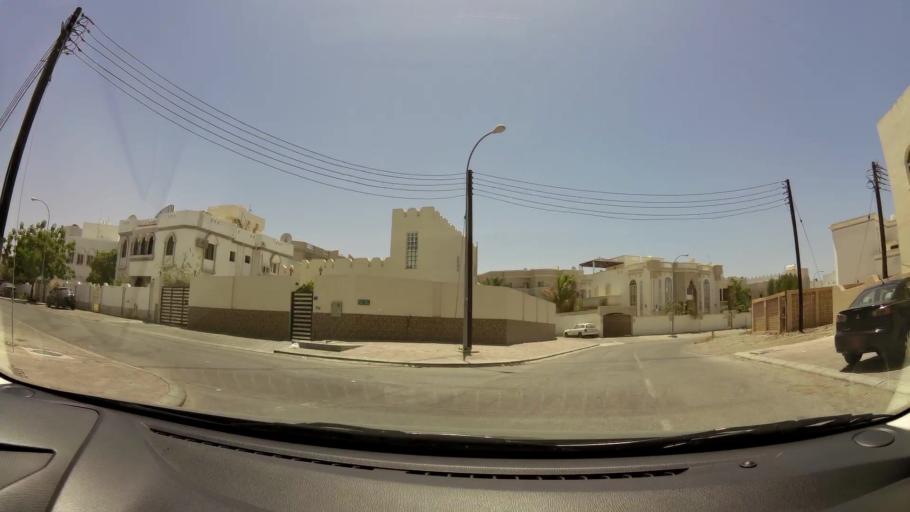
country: OM
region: Muhafazat Masqat
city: Bawshar
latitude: 23.5939
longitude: 58.3767
